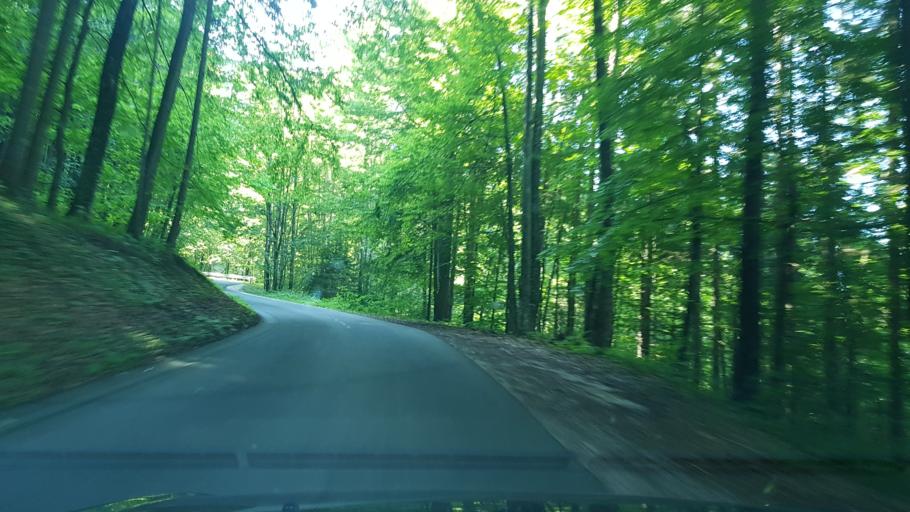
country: SI
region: Ravne na Koroskem
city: Kotlje
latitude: 46.5047
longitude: 14.9582
